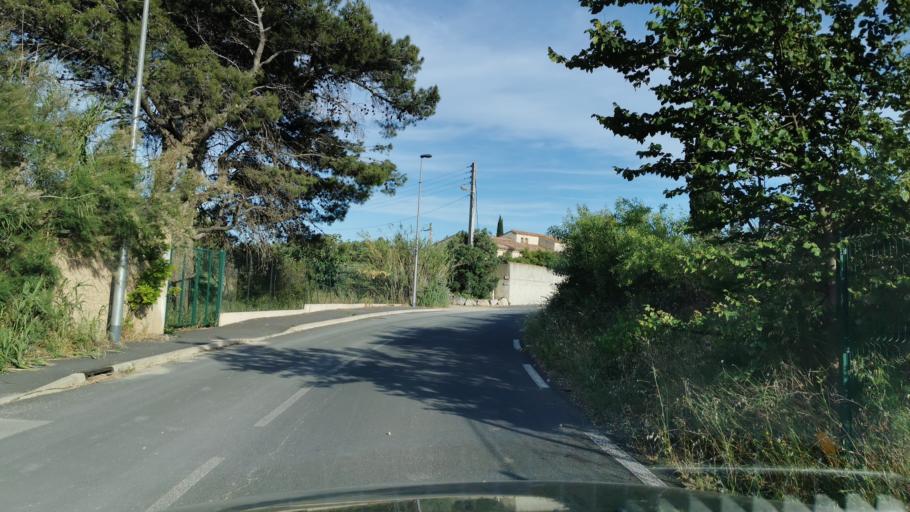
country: FR
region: Languedoc-Roussillon
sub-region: Departement de l'Aude
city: Narbonne
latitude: 43.1691
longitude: 2.9954
